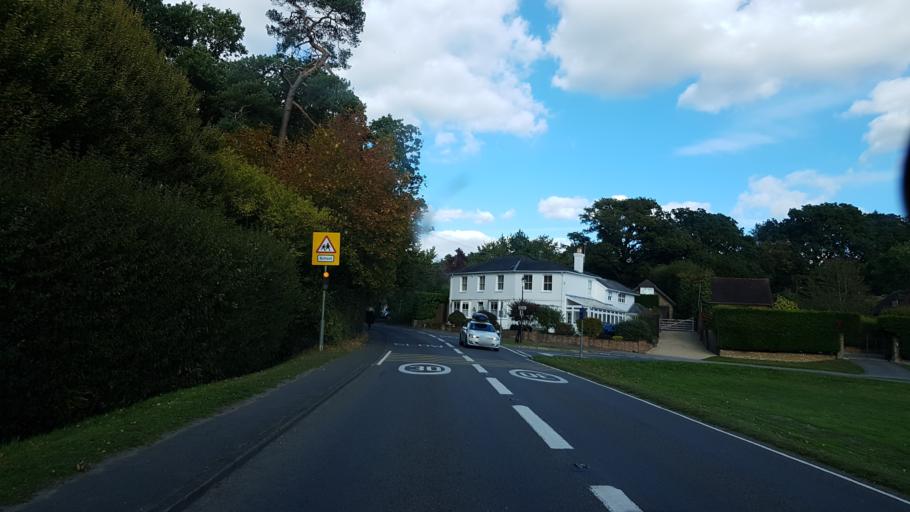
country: GB
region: England
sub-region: Surrey
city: Chiddingfold
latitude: 51.1109
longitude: -0.6285
